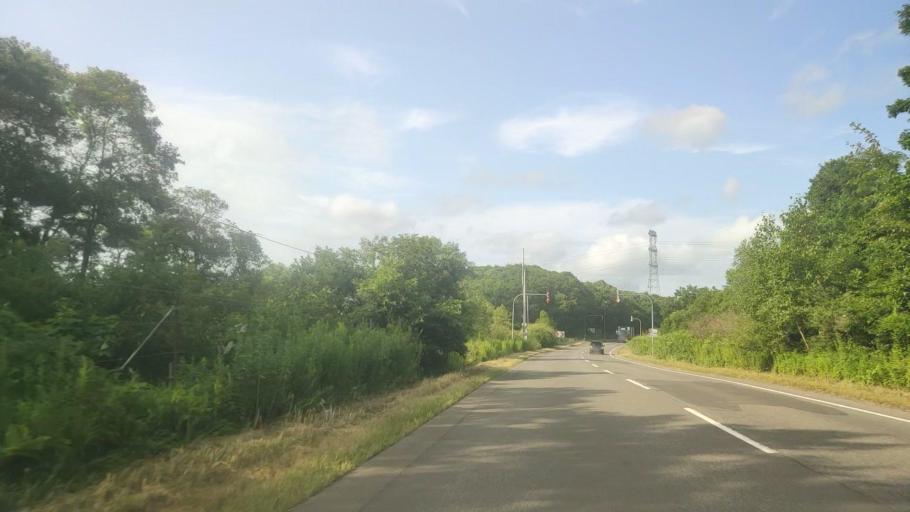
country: JP
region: Hokkaido
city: Chitose
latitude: 42.7067
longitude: 141.7442
